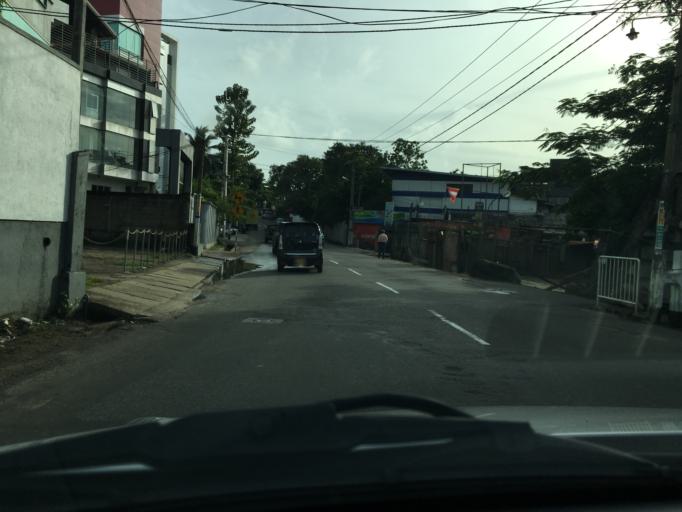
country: LK
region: Western
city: Pita Kotte
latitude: 6.8838
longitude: 79.9002
